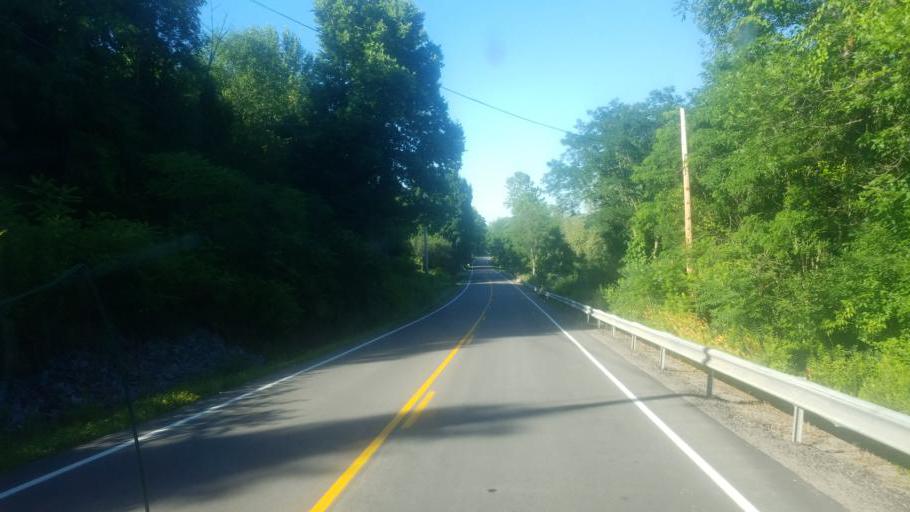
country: US
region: New York
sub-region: Wayne County
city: Newark
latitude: 43.0847
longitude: -77.0681
